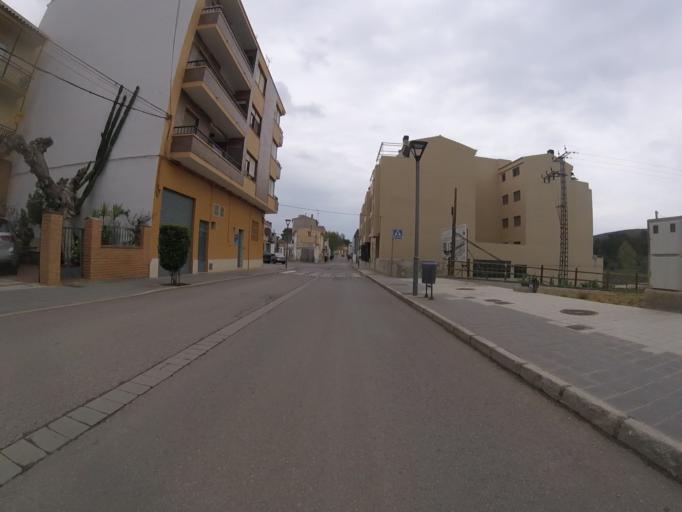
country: ES
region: Valencia
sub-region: Provincia de Castello
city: Cuevas de Vinroma
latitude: 40.3129
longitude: 0.1215
